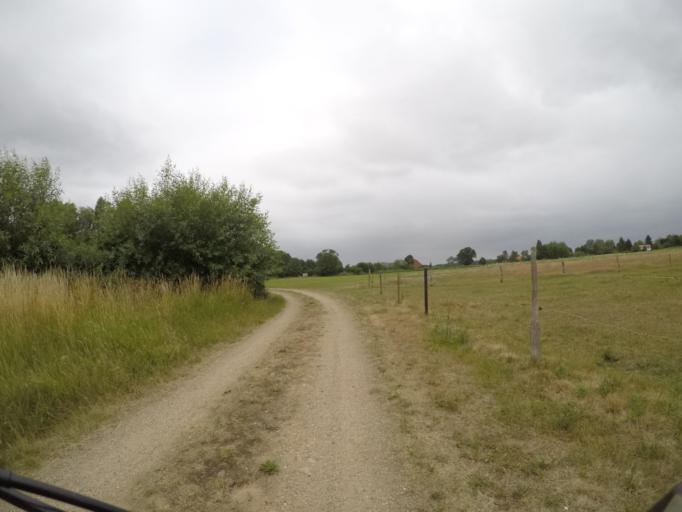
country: DE
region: Lower Saxony
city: Hitzacker
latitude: 53.1914
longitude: 11.0412
